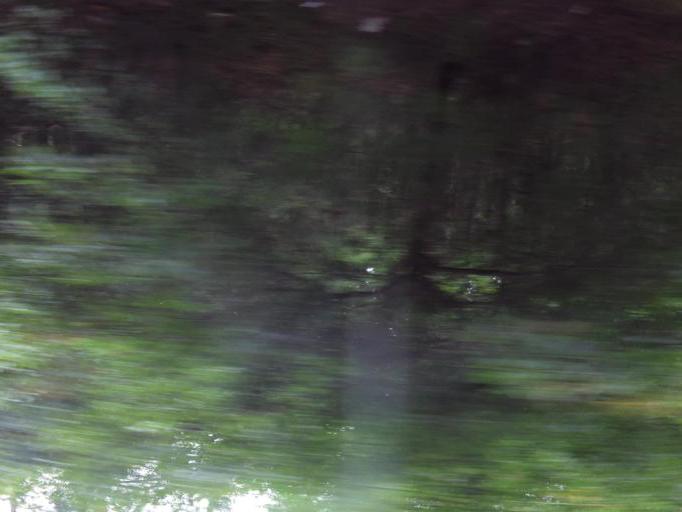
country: US
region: Florida
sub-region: Nassau County
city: Nassau Village-Ratliff
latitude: 30.5493
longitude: -81.7307
